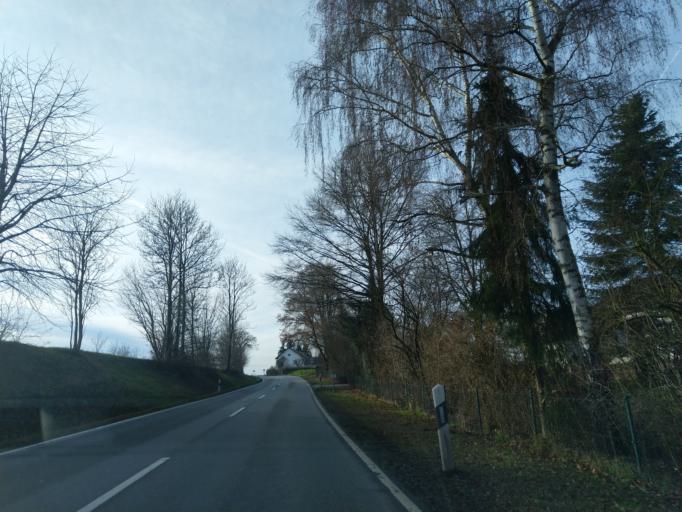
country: DE
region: Bavaria
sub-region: Lower Bavaria
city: Osterhofen
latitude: 48.7003
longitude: 12.9984
